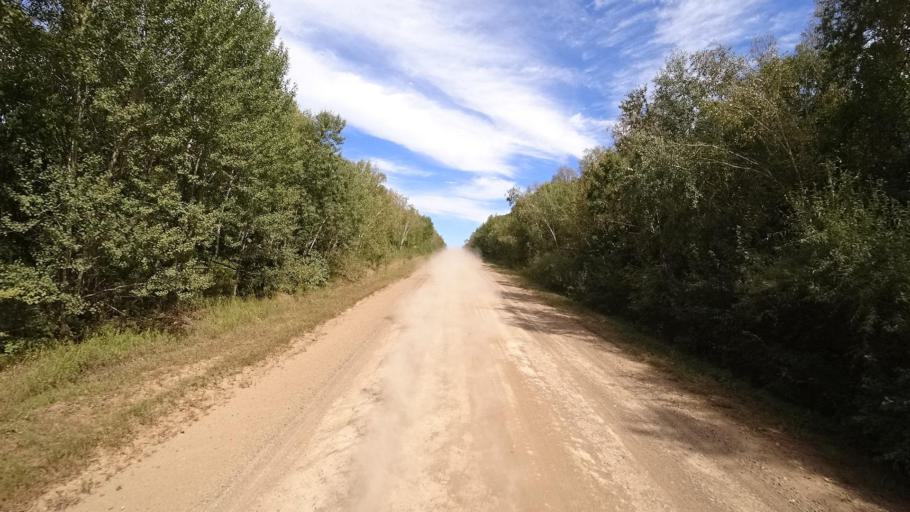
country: RU
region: Primorskiy
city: Yakovlevka
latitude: 44.7015
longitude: 133.6338
